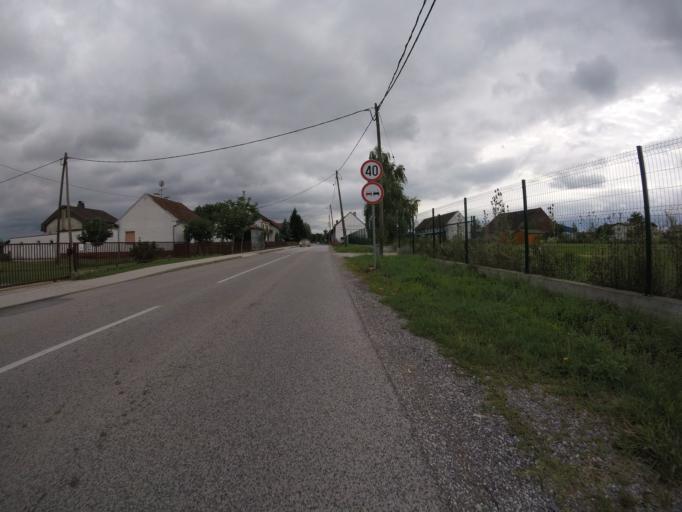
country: HR
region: Zagrebacka
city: Gradici
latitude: 45.7074
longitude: 16.0406
